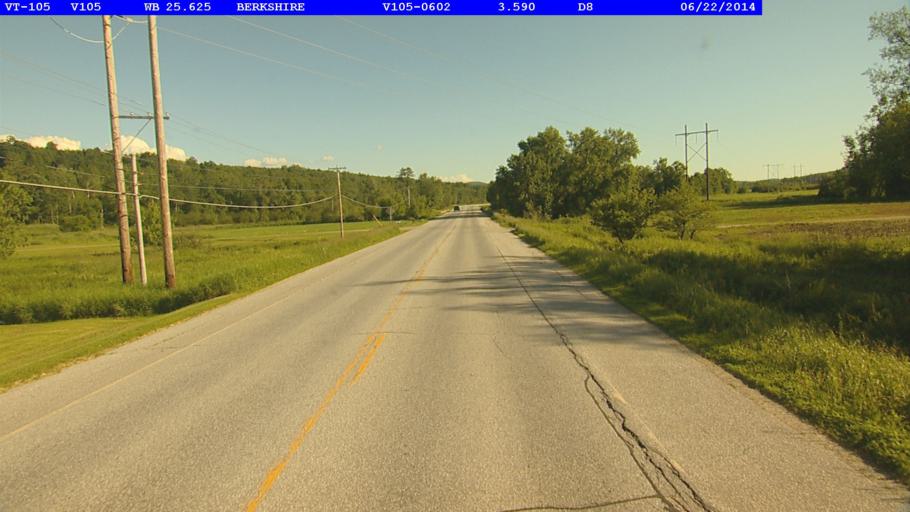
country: US
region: Vermont
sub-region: Franklin County
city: Richford
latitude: 44.9700
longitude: -72.6892
